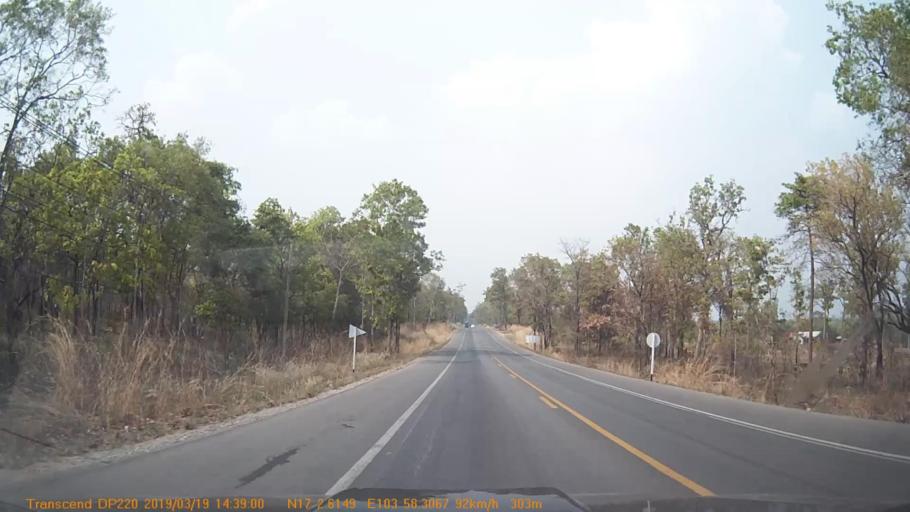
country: TH
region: Sakon Nakhon
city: Phu Phan
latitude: 17.0439
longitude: 103.9718
